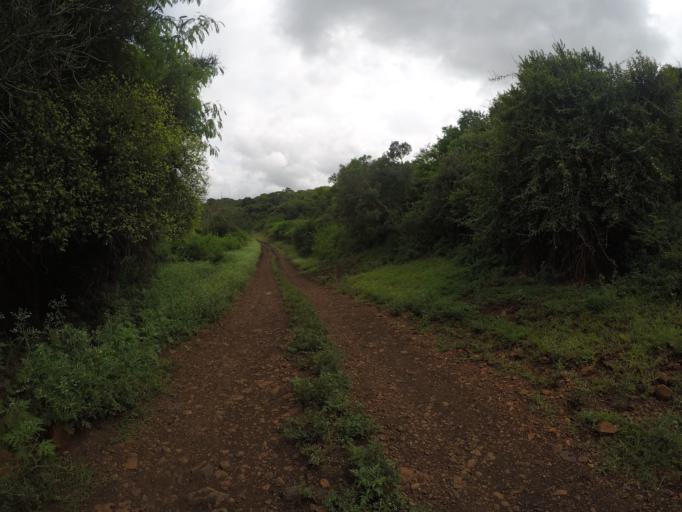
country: ZA
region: KwaZulu-Natal
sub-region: uThungulu District Municipality
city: Empangeni
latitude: -28.5901
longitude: 31.8727
